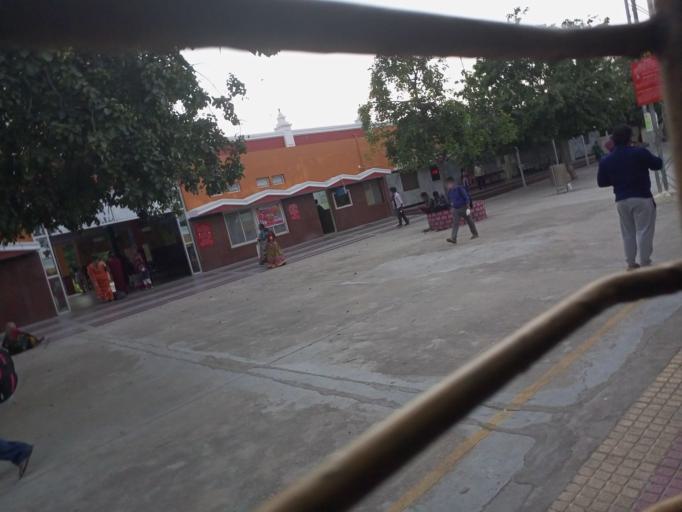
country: IN
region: Andhra Pradesh
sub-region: Anantapur
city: Dharmavaram
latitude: 14.4262
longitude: 77.7153
